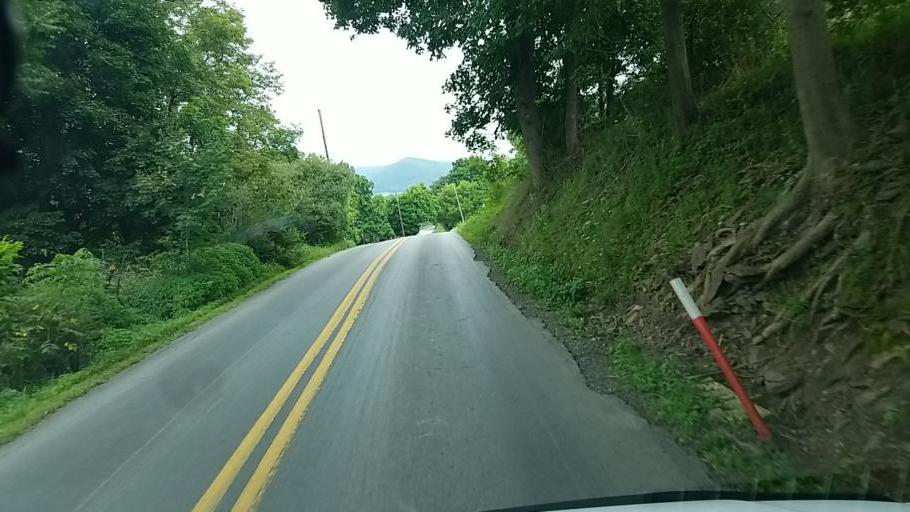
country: US
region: Pennsylvania
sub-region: Dauphin County
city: Elizabethville
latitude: 40.5798
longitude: -76.8044
